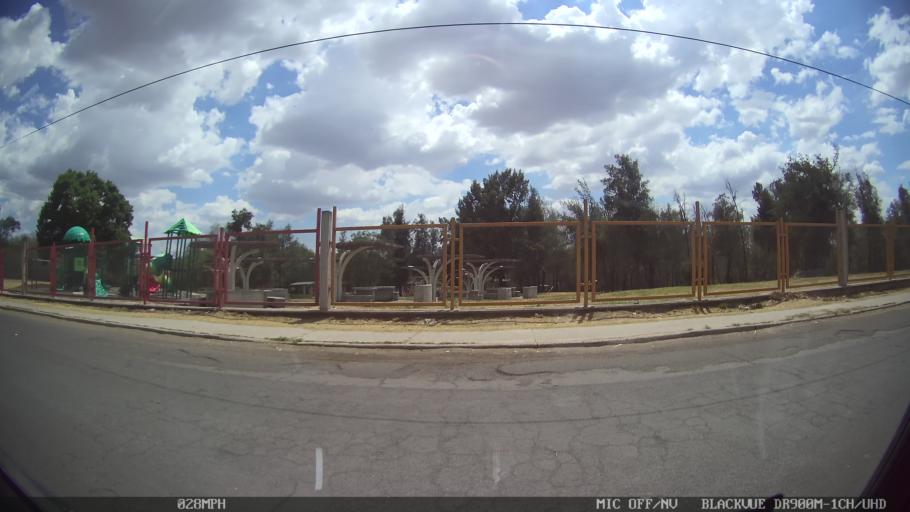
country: MX
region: Jalisco
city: Tlaquepaque
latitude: 20.6729
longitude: -103.2644
